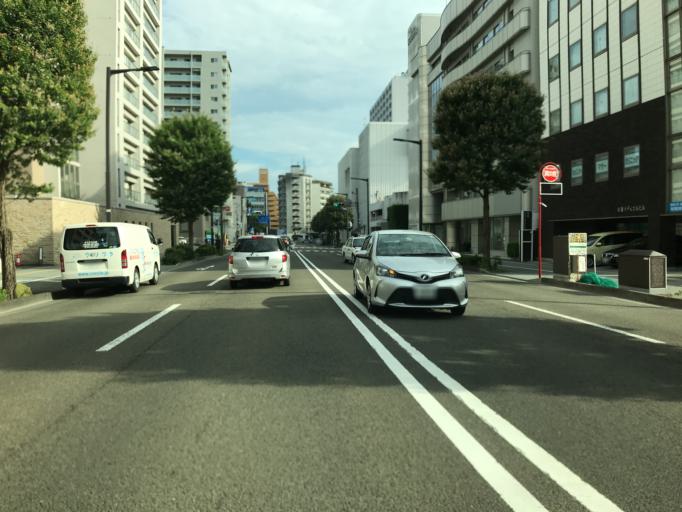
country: JP
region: Miyagi
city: Sendai-shi
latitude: 38.2668
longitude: 140.8629
